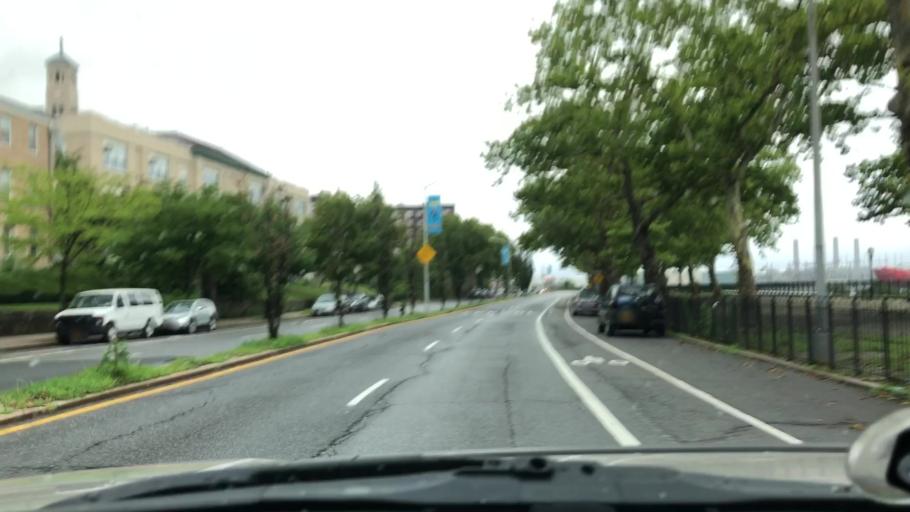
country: US
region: New Jersey
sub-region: Hudson County
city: Bayonne
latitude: 40.6477
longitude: -74.0823
